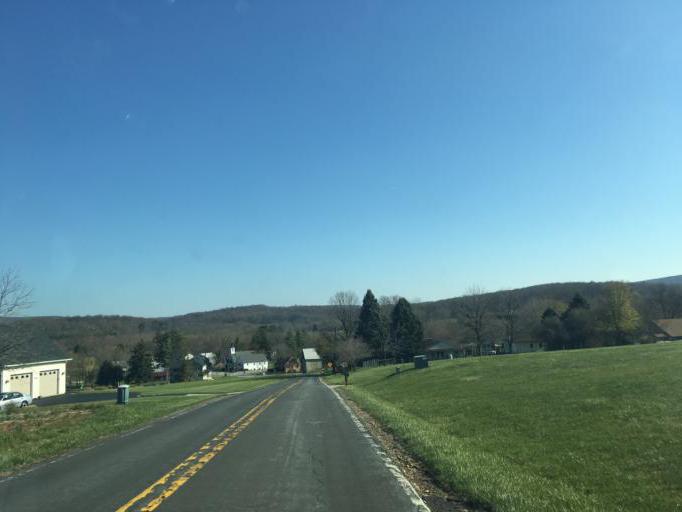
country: US
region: Maryland
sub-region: Frederick County
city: Myersville
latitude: 39.5706
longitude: -77.5515
